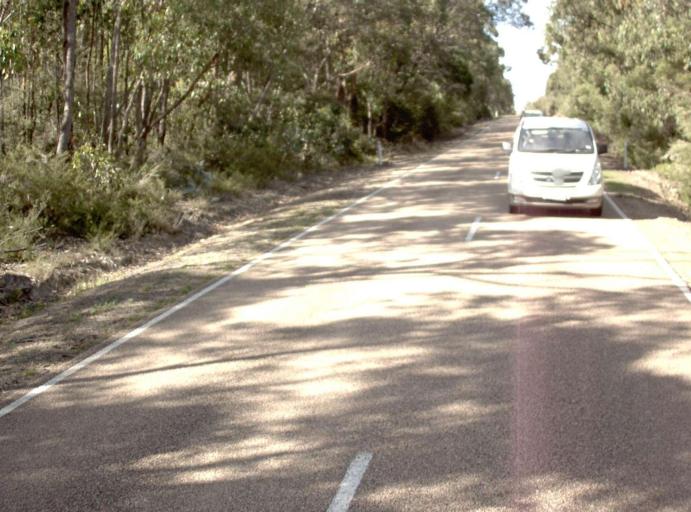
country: AU
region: Victoria
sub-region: East Gippsland
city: Lakes Entrance
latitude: -37.6132
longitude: 148.1152
